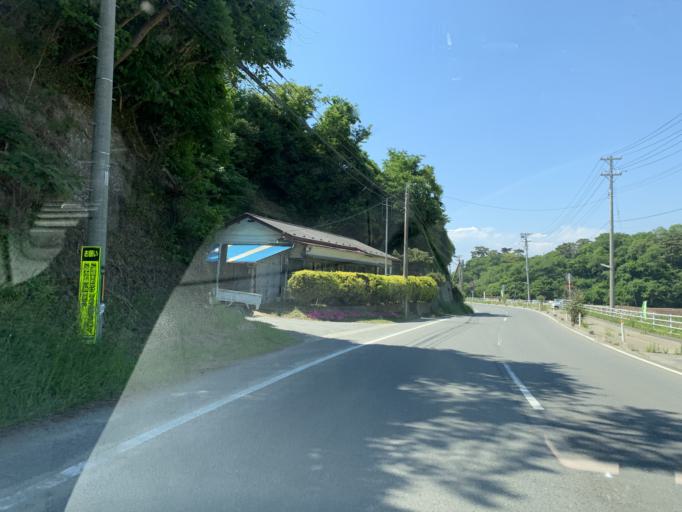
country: JP
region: Miyagi
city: Matsushima
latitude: 38.3361
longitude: 141.1502
